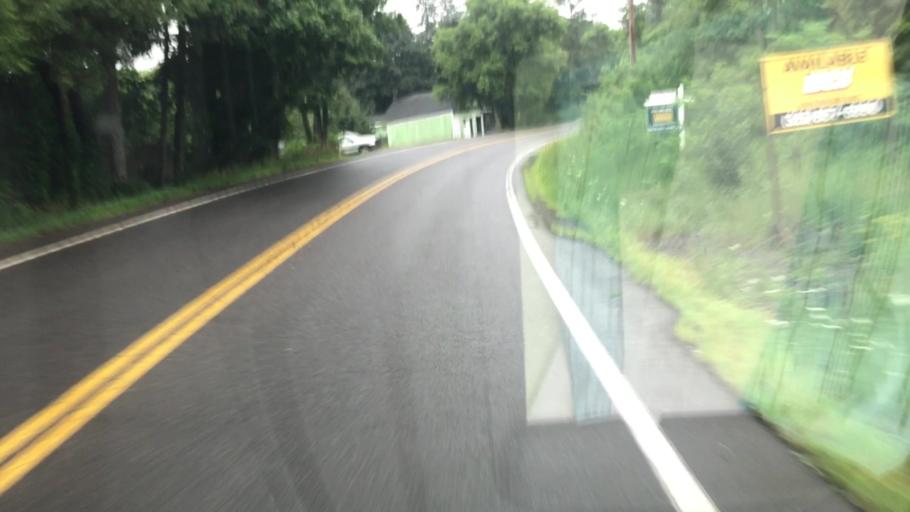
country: US
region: New York
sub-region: Onondaga County
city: Manlius
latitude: 42.9987
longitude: -75.9896
